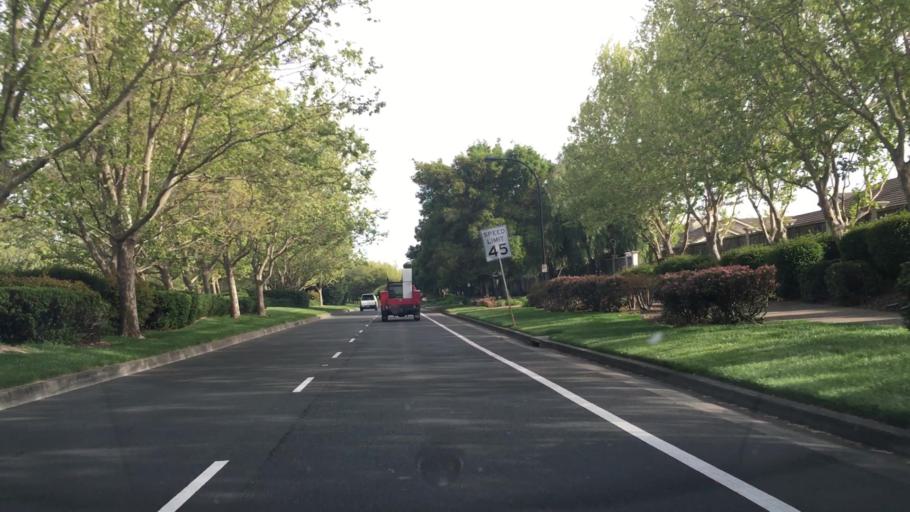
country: US
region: California
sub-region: Solano County
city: Green Valley
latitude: 38.2219
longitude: -122.1443
